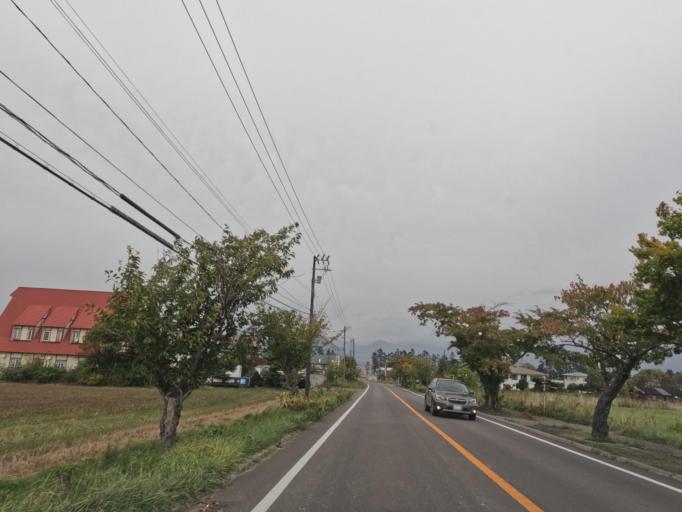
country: JP
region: Hokkaido
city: Date
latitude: 42.5548
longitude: 140.8626
